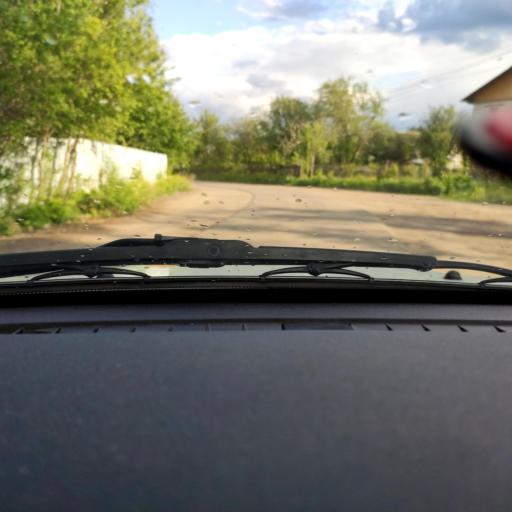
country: RU
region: Voronezj
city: Shilovo
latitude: 51.5853
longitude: 39.1594
